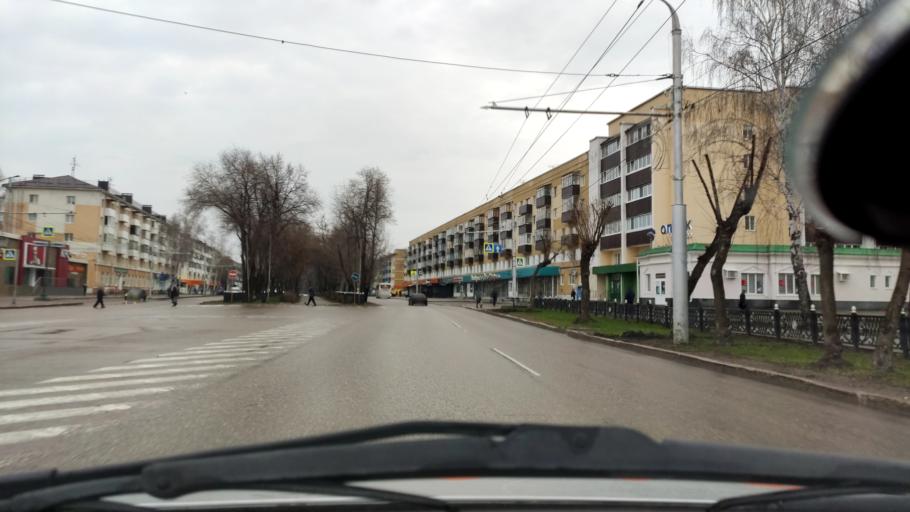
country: RU
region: Bashkortostan
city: Sterlitamak
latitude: 53.6380
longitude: 55.9375
